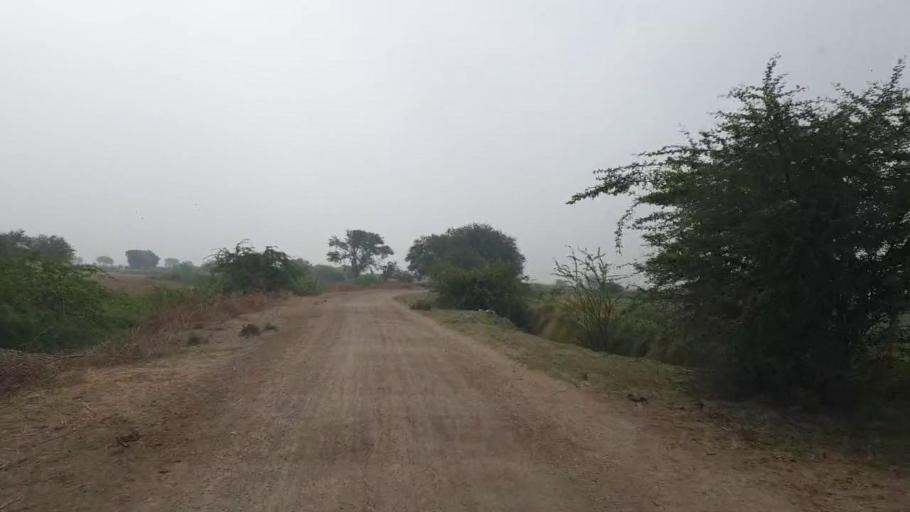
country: PK
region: Sindh
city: Badin
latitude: 24.5874
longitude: 68.6796
